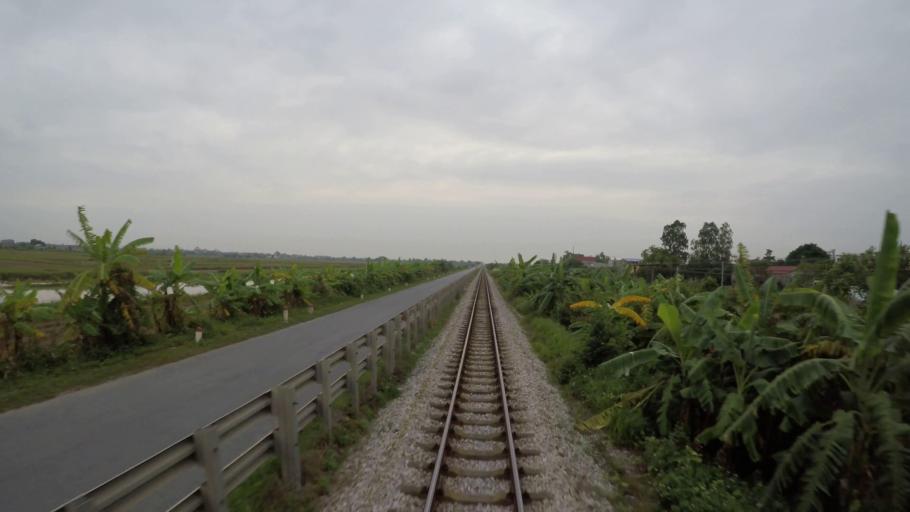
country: VN
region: Hung Yen
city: Ban Yen Nhan
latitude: 20.9795
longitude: 106.0823
